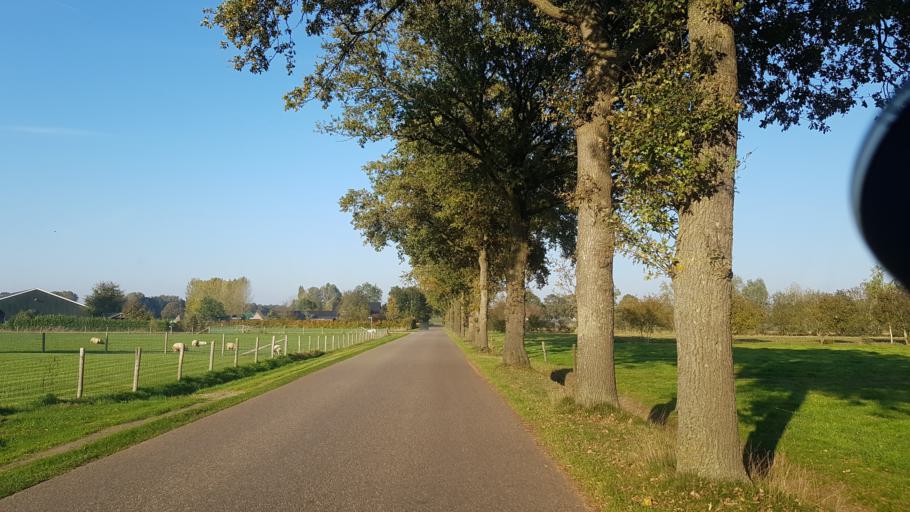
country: NL
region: Gelderland
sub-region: Gemeente Apeldoorn
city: Loenen
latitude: 52.1827
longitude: 6.0297
